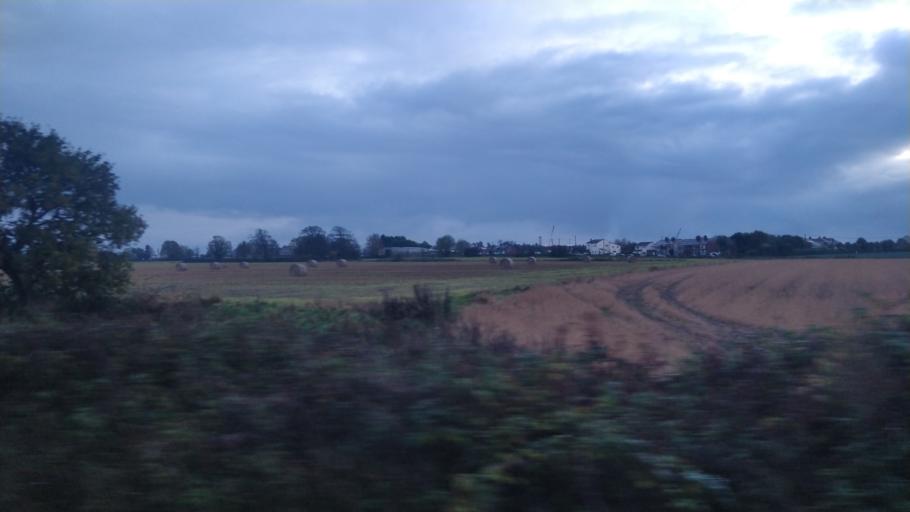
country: GB
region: England
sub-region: Lancashire
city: Ormskirk
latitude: 53.6100
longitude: -2.8613
